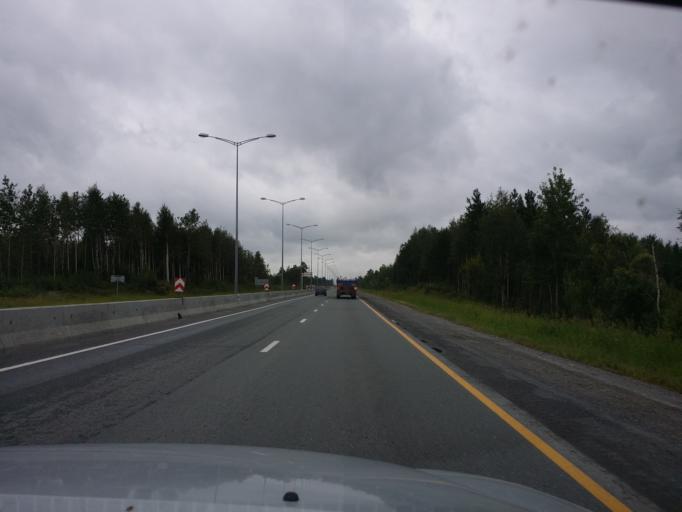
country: RU
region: Khanty-Mansiyskiy Avtonomnyy Okrug
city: Nizhnevartovsk
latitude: 61.0061
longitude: 76.4092
